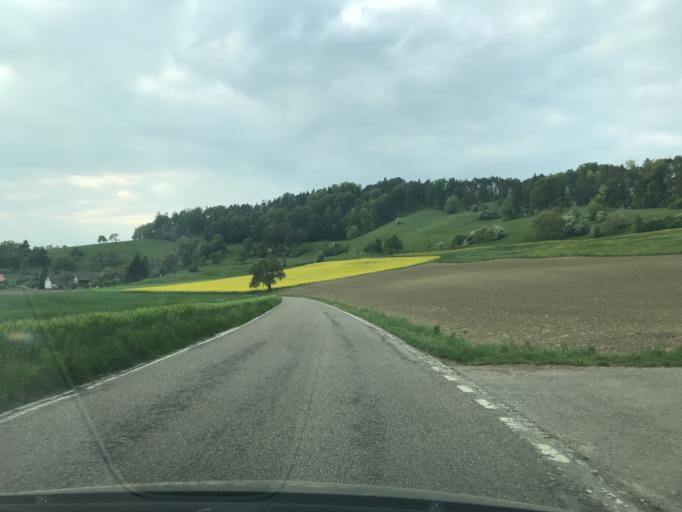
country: CH
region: Zurich
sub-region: Bezirk Winterthur
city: Wuelflingen (Kreis 6) / Oberfeld
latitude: 47.4931
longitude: 8.6867
